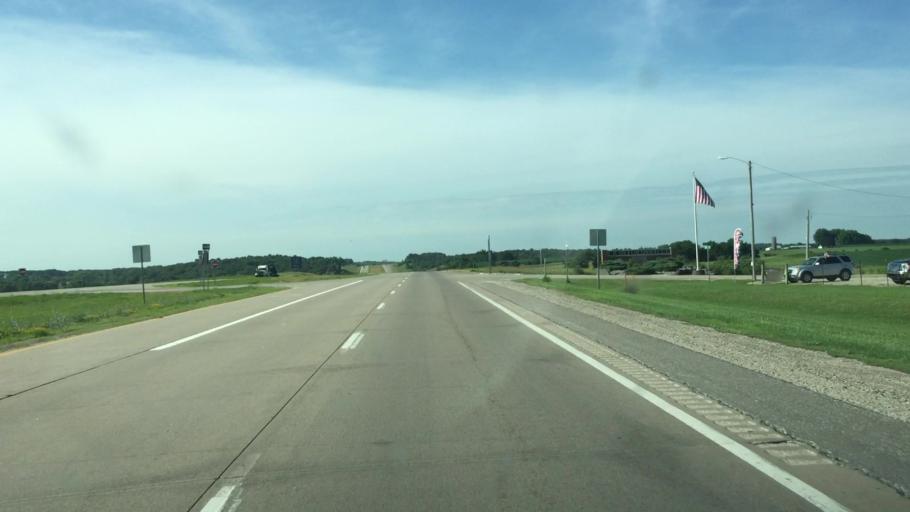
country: US
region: Iowa
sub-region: Henry County
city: Winfield
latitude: 41.2145
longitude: -91.5301
